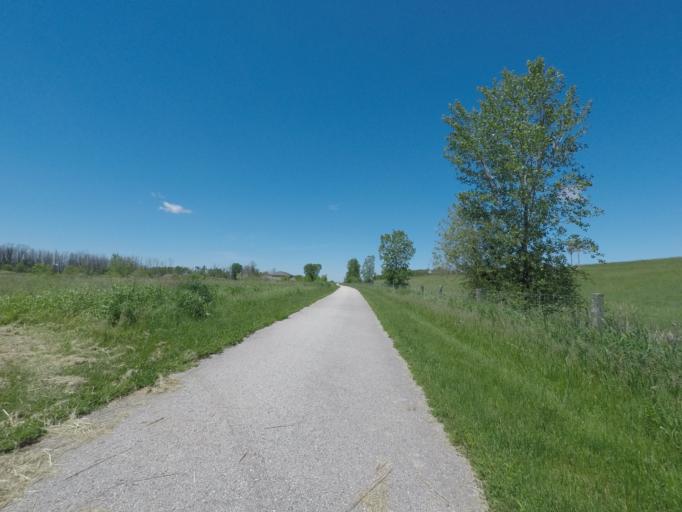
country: US
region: Wisconsin
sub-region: Sheboygan County
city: Sheboygan Falls
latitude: 43.7498
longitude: -87.8219
